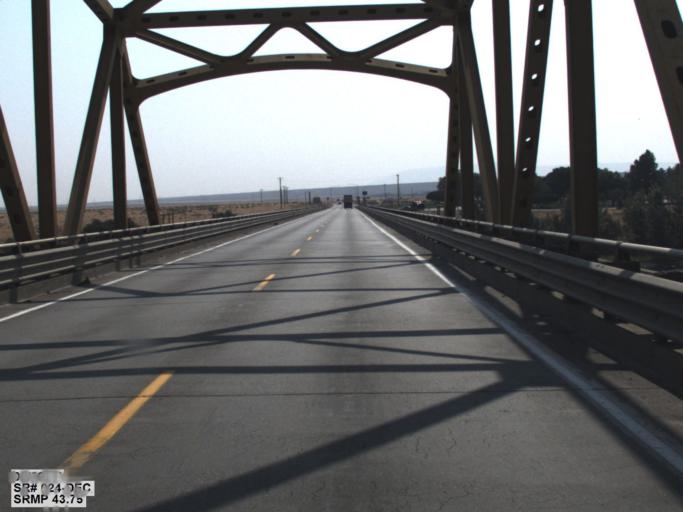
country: US
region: Washington
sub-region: Grant County
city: Desert Aire
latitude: 46.6418
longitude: -119.7323
